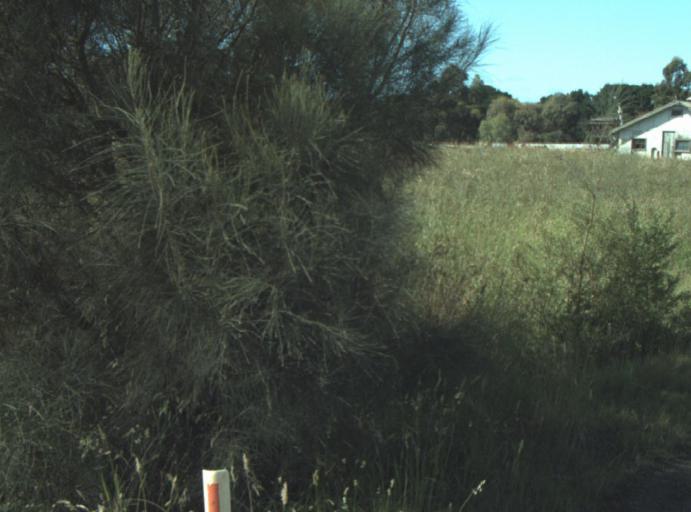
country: AU
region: Victoria
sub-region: Greater Geelong
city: Clifton Springs
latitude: -38.2165
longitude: 144.5940
